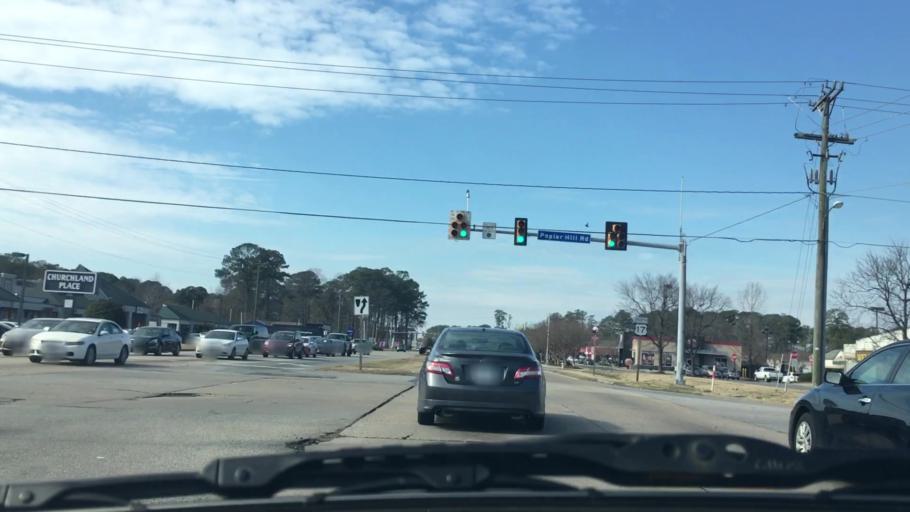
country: US
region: Virginia
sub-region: City of Portsmouth
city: Portsmouth Heights
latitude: 36.8622
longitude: -76.4011
